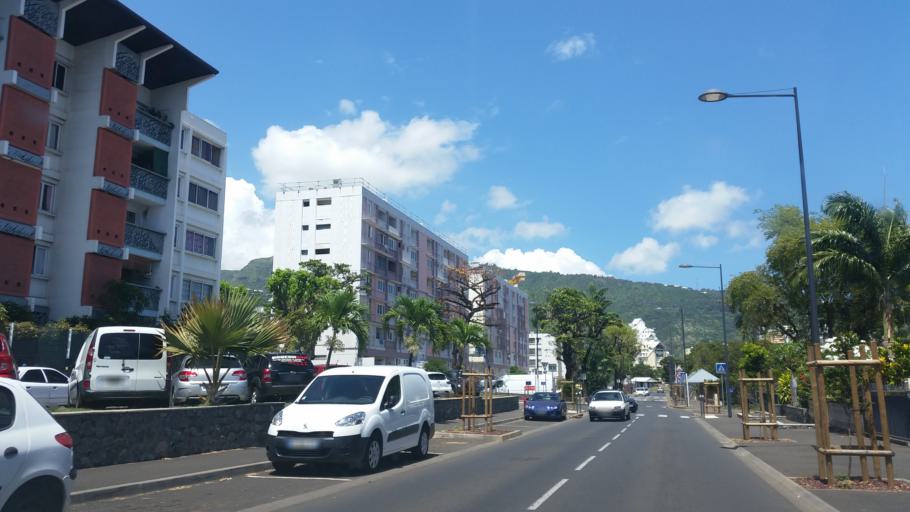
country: RE
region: Reunion
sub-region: Reunion
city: Saint-Denis
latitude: -20.8926
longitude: 55.4632
